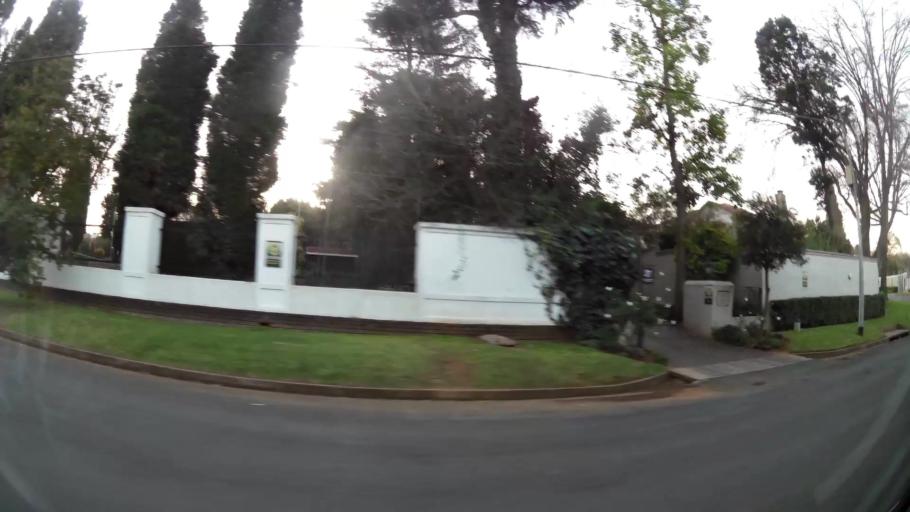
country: ZA
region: Gauteng
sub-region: City of Johannesburg Metropolitan Municipality
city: Johannesburg
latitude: -26.1404
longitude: 28.0576
